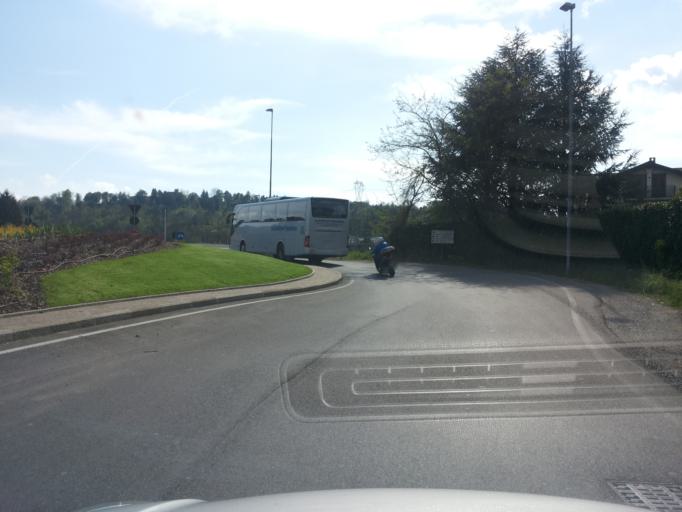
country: IT
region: Lombardy
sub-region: Provincia di Como
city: Rodero
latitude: 45.8386
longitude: 8.9100
